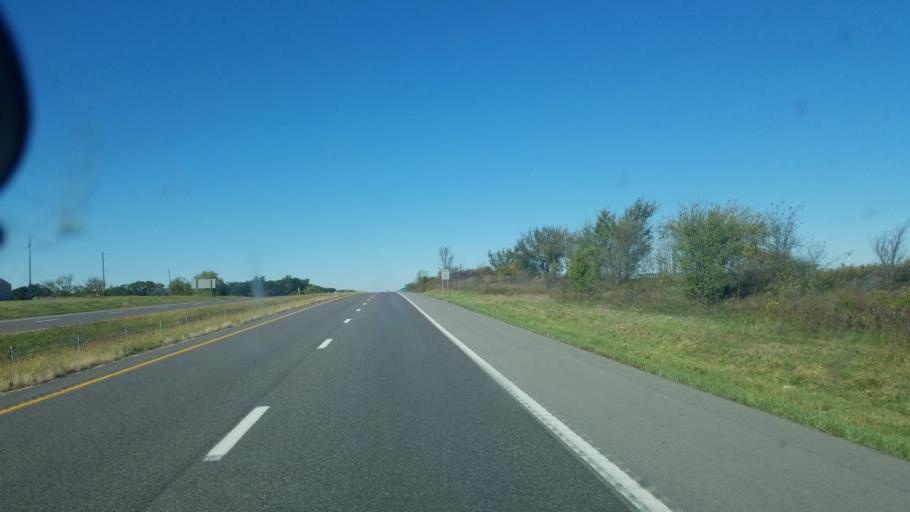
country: US
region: Missouri
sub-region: Saline County
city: Marshall
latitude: 38.9538
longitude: -93.0975
